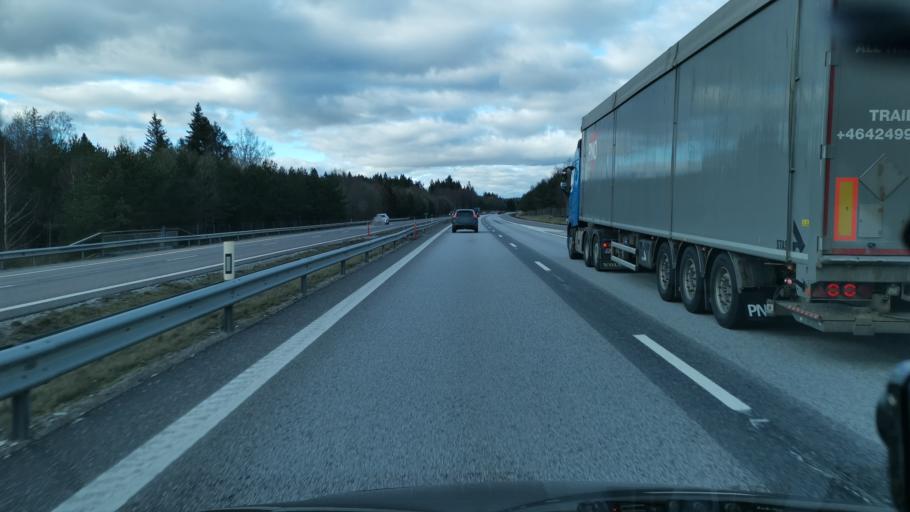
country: SE
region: Vaestra Goetaland
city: Svanesund
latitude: 58.1165
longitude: 11.8800
